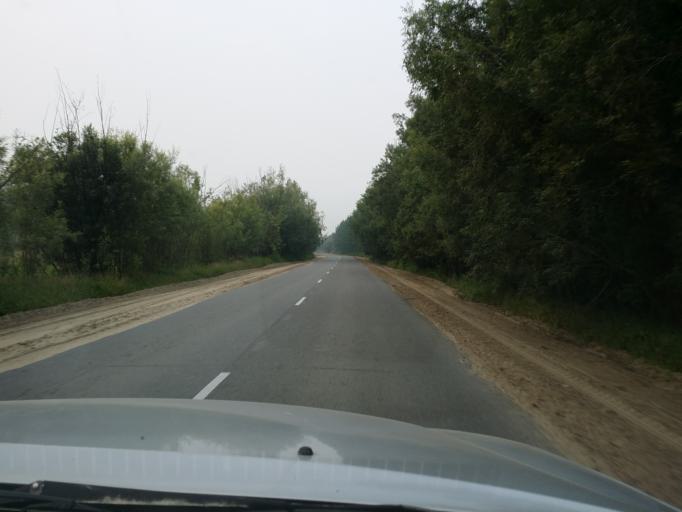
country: RU
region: Khanty-Mansiyskiy Avtonomnyy Okrug
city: Megion
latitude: 61.0040
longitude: 76.3082
